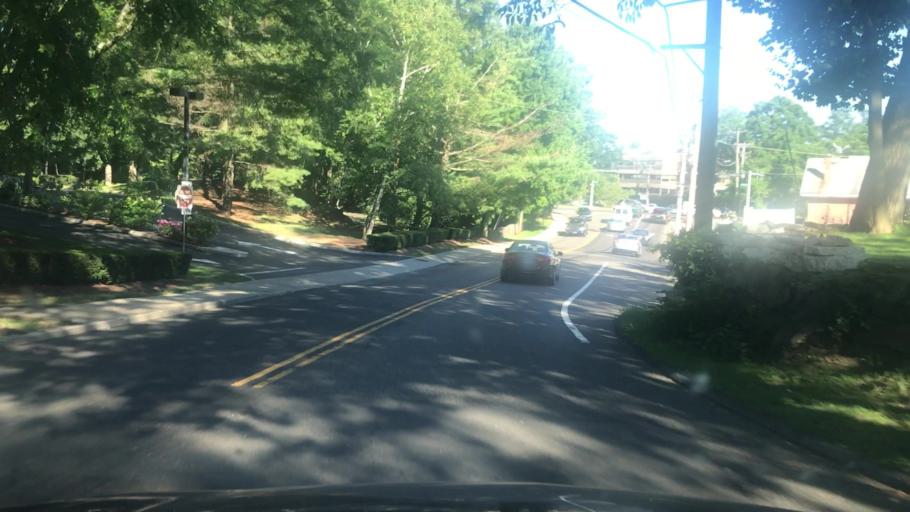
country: US
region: Connecticut
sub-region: Fairfield County
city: Pemberwick
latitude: 41.0173
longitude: -73.6501
